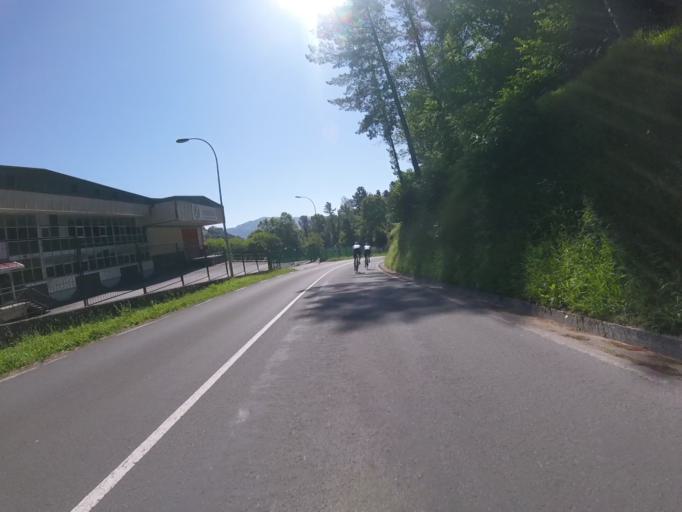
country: ES
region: Basque Country
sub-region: Provincia de Guipuzcoa
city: Albiztur
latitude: 43.1246
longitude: -2.1189
